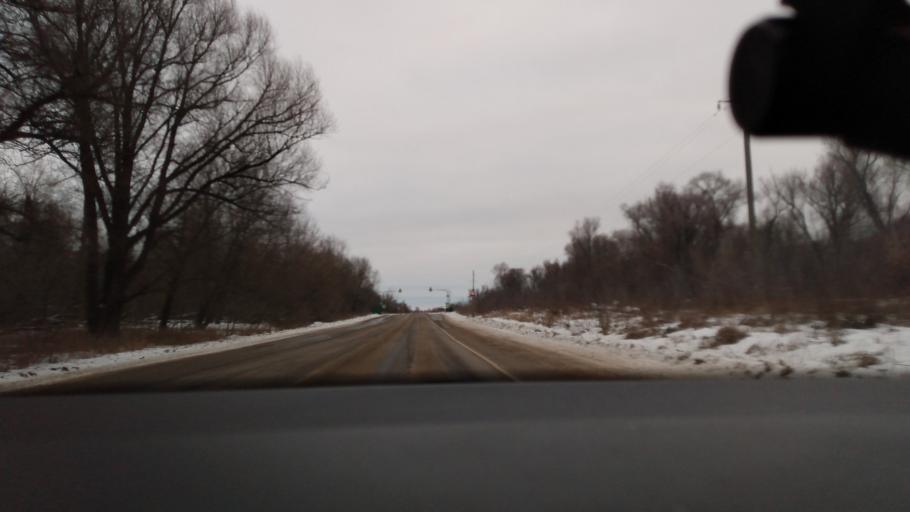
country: RU
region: Moskovskaya
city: Krasnaya Poyma
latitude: 55.0959
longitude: 39.1465
